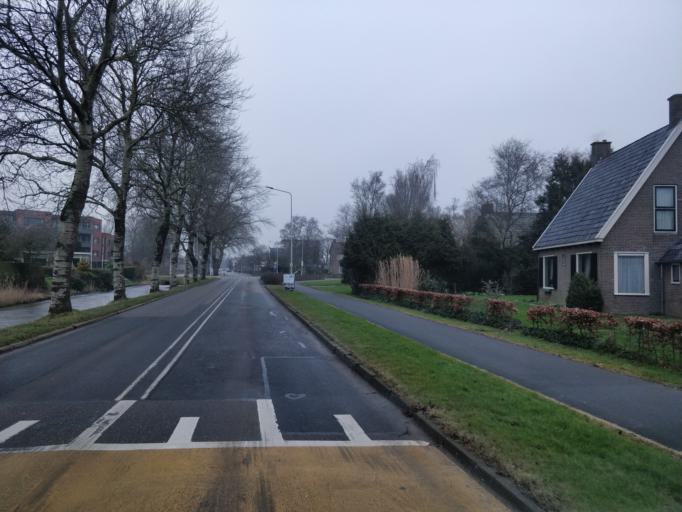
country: NL
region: Friesland
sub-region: Gemeente Het Bildt
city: Sint Annaparochie
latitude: 53.2722
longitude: 5.6581
